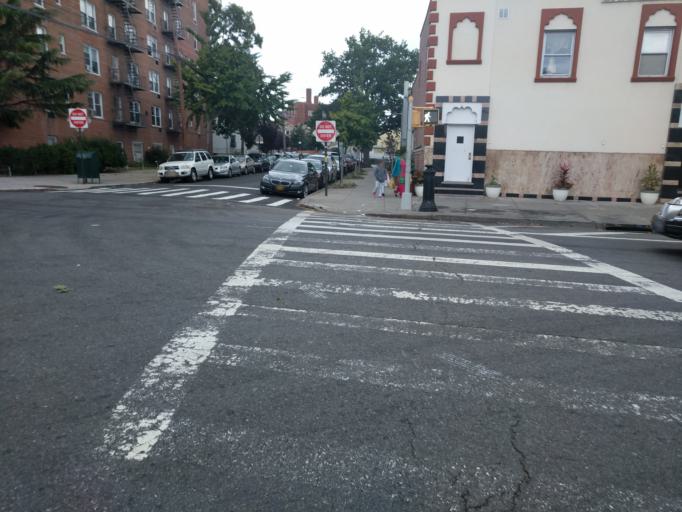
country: US
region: New York
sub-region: Queens County
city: Long Island City
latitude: 40.7507
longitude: -73.9010
